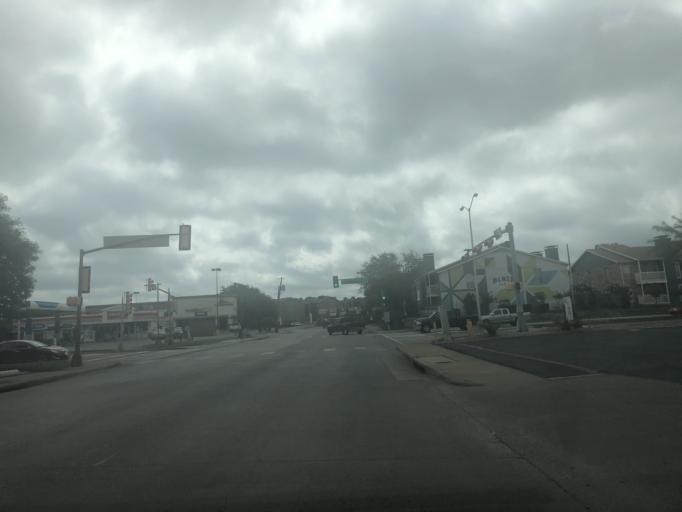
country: US
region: Texas
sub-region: Dallas County
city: University Park
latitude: 32.8634
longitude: -96.8657
